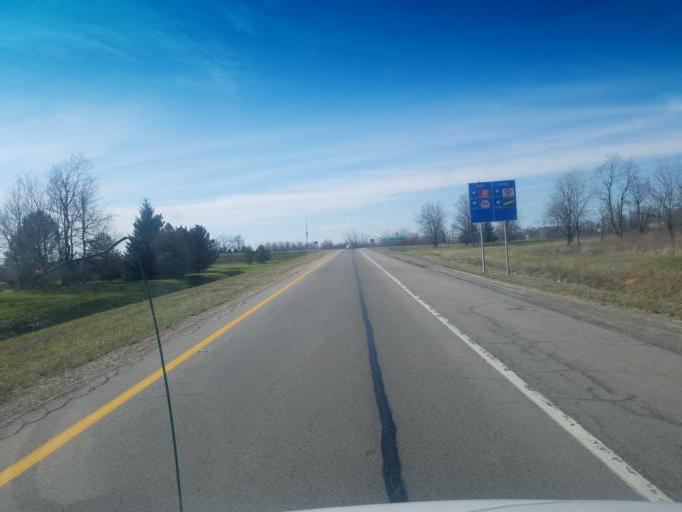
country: US
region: Ohio
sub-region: Logan County
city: Bellefontaine
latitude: 40.3681
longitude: -83.7276
